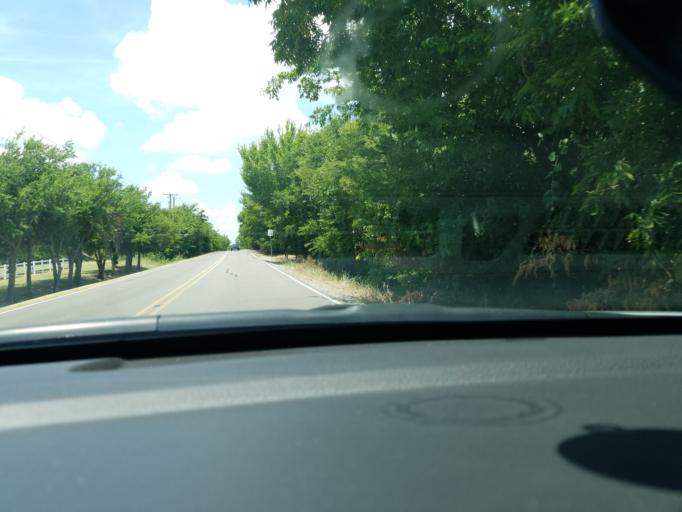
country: US
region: Texas
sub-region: Dallas County
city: Sunnyvale
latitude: 32.8140
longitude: -96.5864
